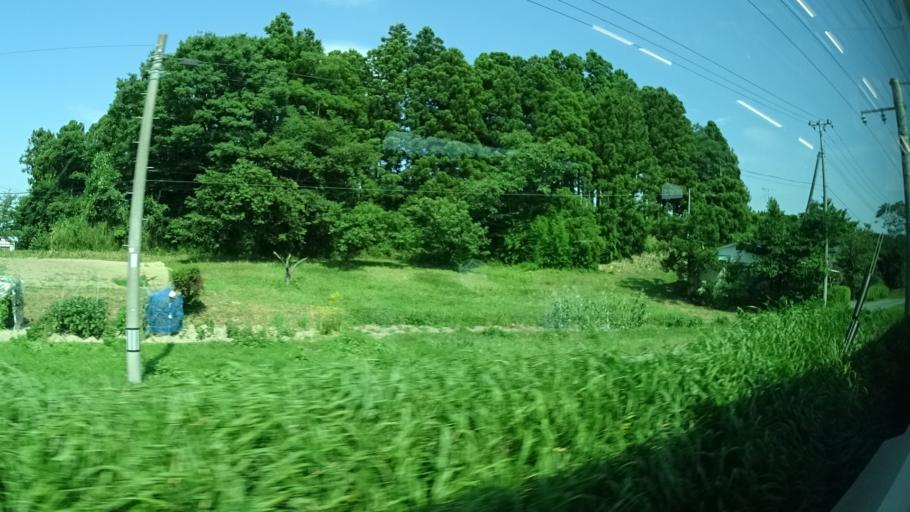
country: JP
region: Miyagi
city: Kogota
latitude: 38.4992
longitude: 141.0851
